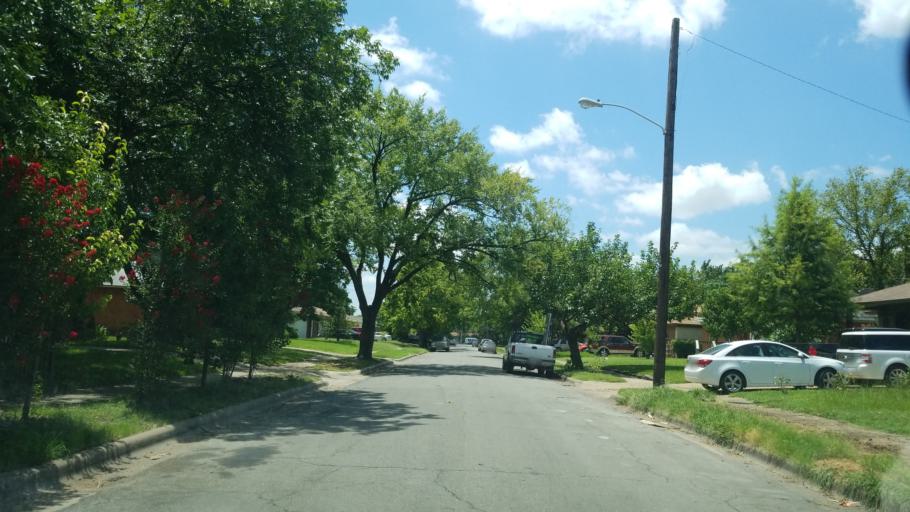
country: US
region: Texas
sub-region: Dallas County
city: Balch Springs
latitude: 32.7434
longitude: -96.6973
